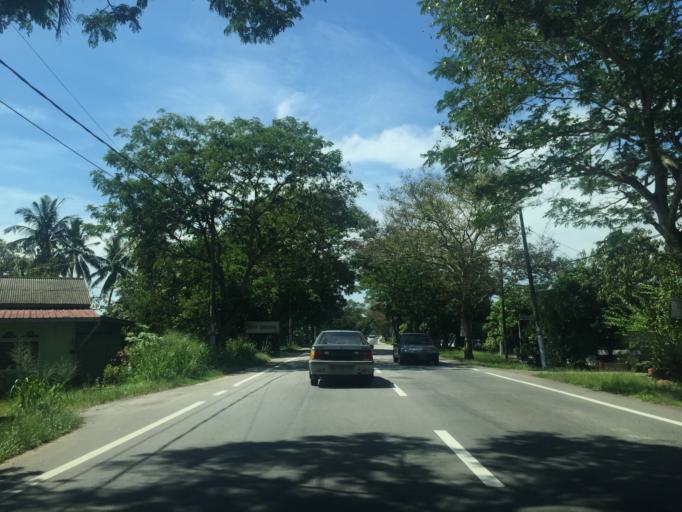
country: MY
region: Penang
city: Tasek Glugor
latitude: 5.4655
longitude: 100.4537
